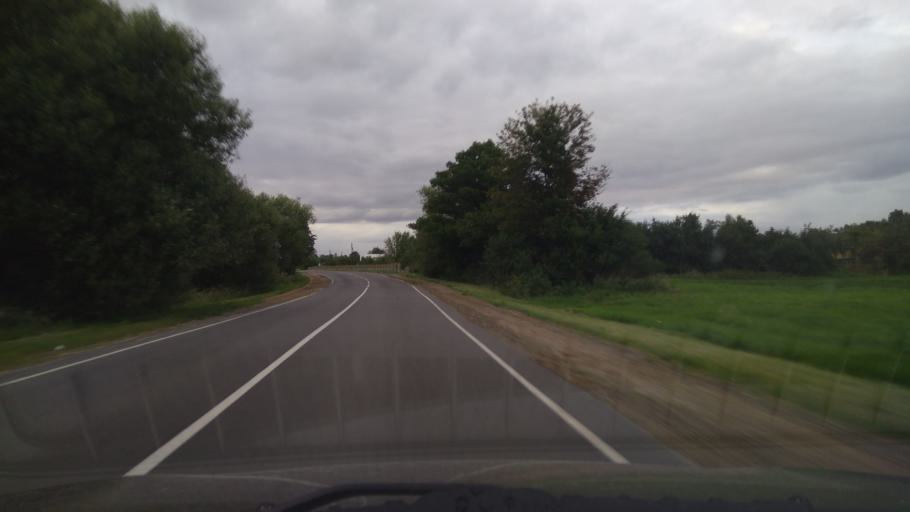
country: BY
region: Brest
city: Byaroza
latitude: 52.4196
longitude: 24.9805
